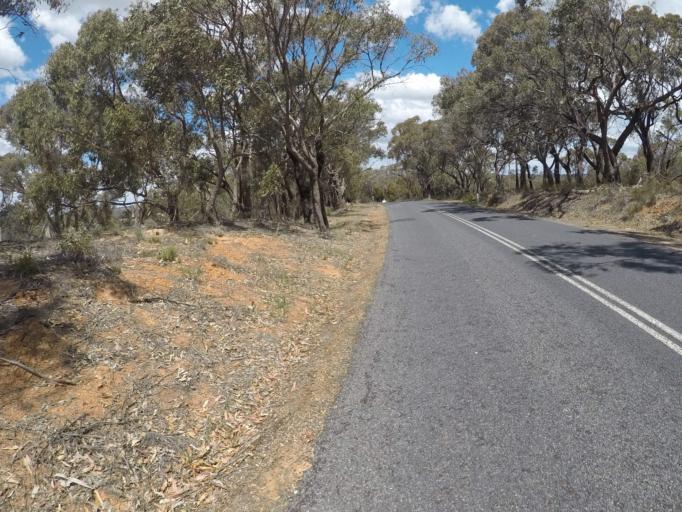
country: AU
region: New South Wales
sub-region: Blayney
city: Blayney
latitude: -33.5832
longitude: 149.3905
